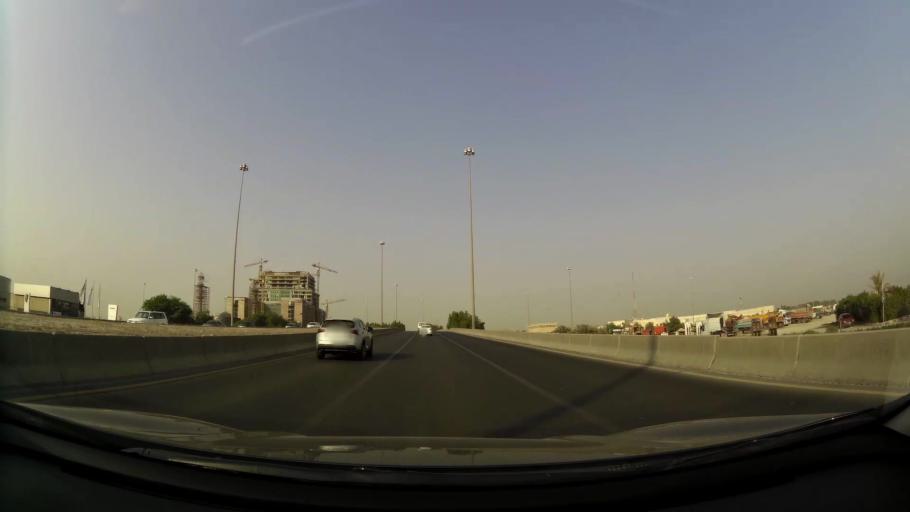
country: KW
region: Al Asimah
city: Ar Rabiyah
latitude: 29.3135
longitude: 47.9282
